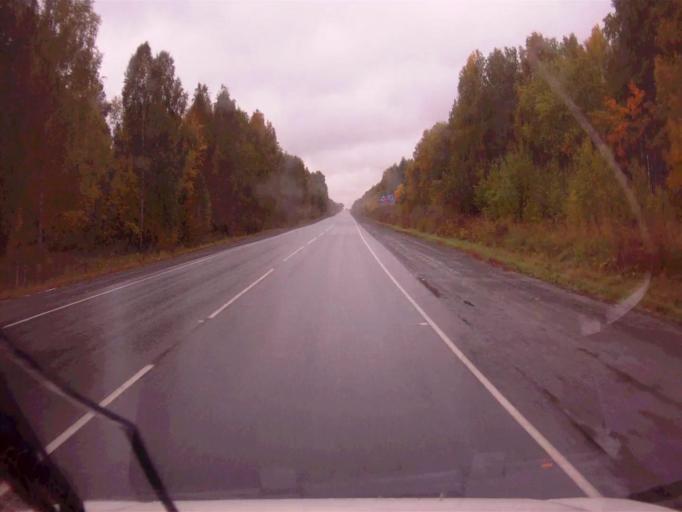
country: RU
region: Chelyabinsk
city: Roshchino
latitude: 55.3725
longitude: 61.1563
